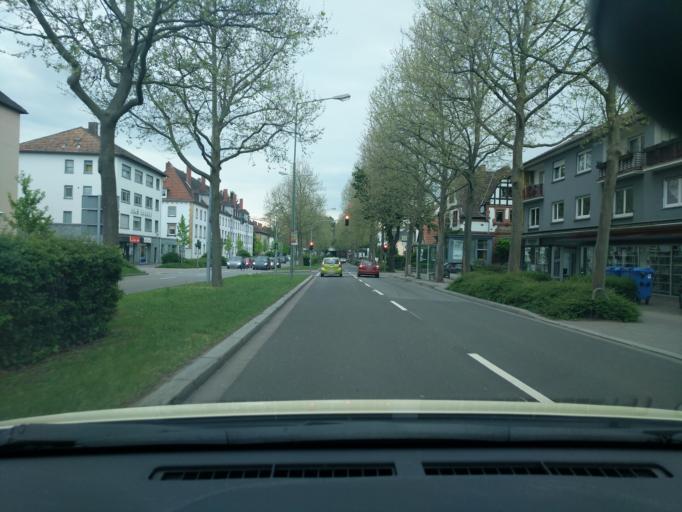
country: DE
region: Rheinland-Pfalz
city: Kaiserslautern
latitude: 49.4450
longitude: 7.7919
